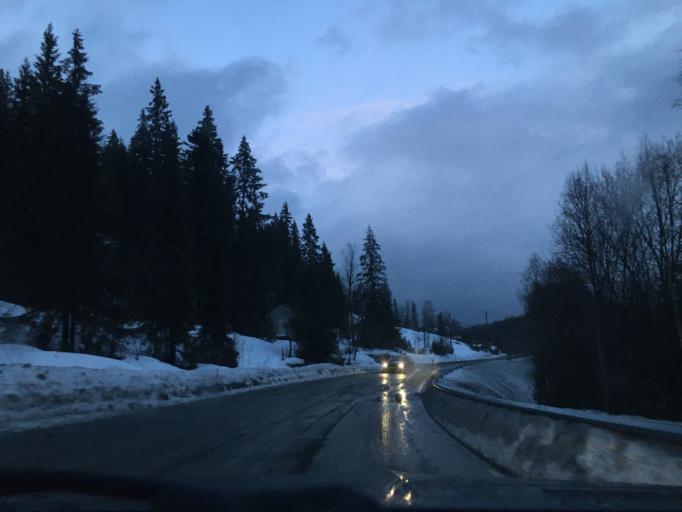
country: NO
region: Nordland
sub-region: Rana
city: Hauknes
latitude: 66.3005
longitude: 13.9304
